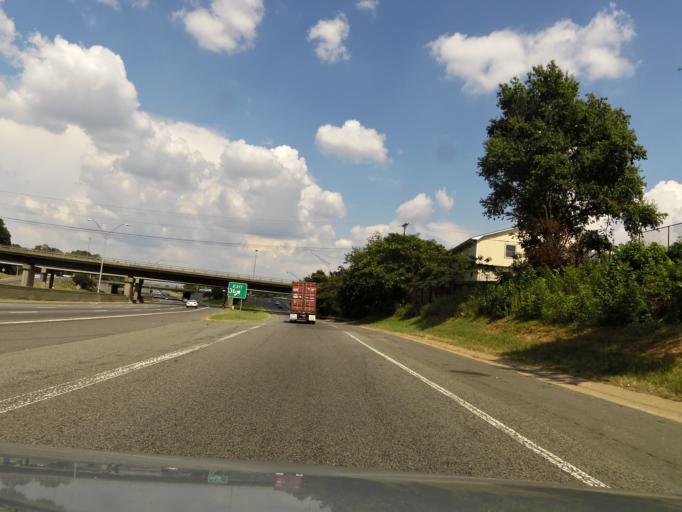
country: US
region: North Carolina
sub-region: Mecklenburg County
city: Charlotte
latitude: 35.2600
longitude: -80.8812
